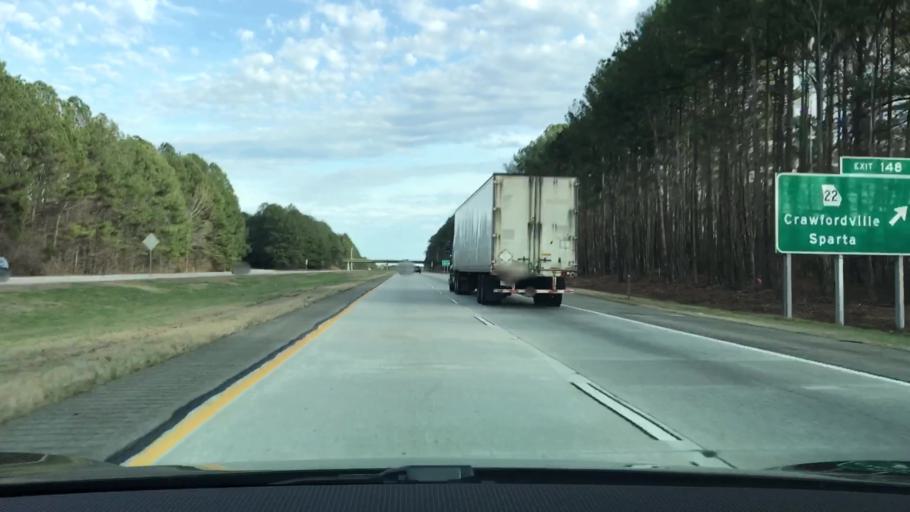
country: US
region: Georgia
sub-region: Taliaferro County
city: Crawfordville
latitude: 33.5300
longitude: -82.9169
